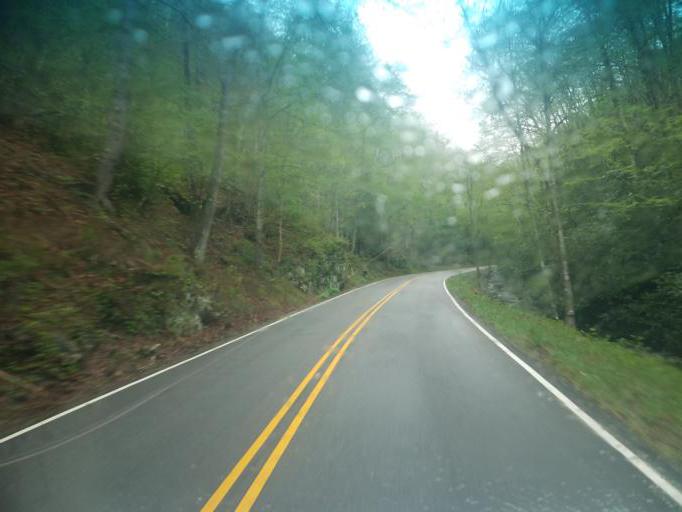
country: US
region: Virginia
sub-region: Washington County
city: Glade Spring
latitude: 36.6458
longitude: -81.7314
